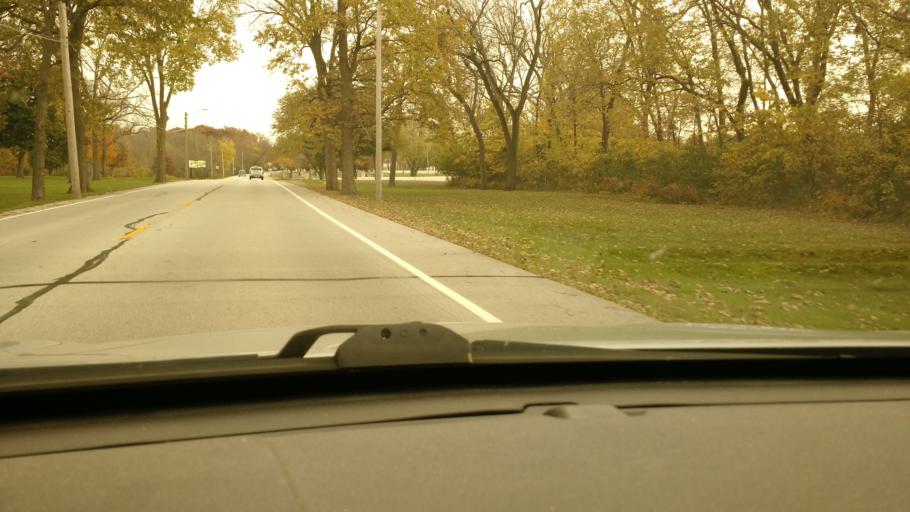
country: US
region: Iowa
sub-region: Scott County
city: Bettendorf
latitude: 41.5161
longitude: -90.5262
